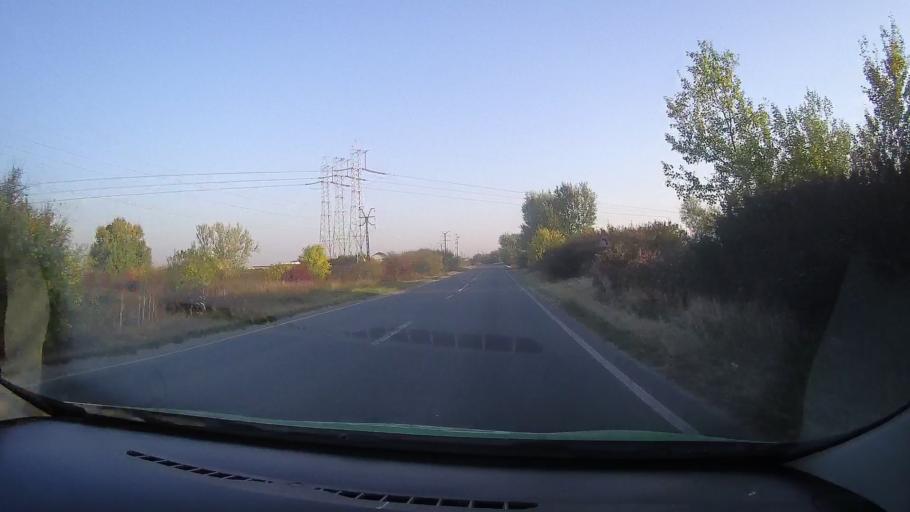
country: RO
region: Arad
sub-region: Comuna Sofronea
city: Sofronea
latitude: 46.2360
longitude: 21.3211
